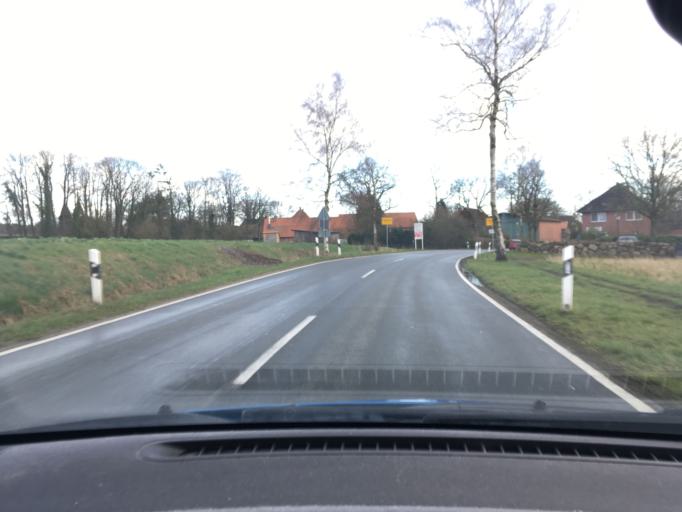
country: DE
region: Lower Saxony
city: Egestorf
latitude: 53.2134
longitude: 10.0296
